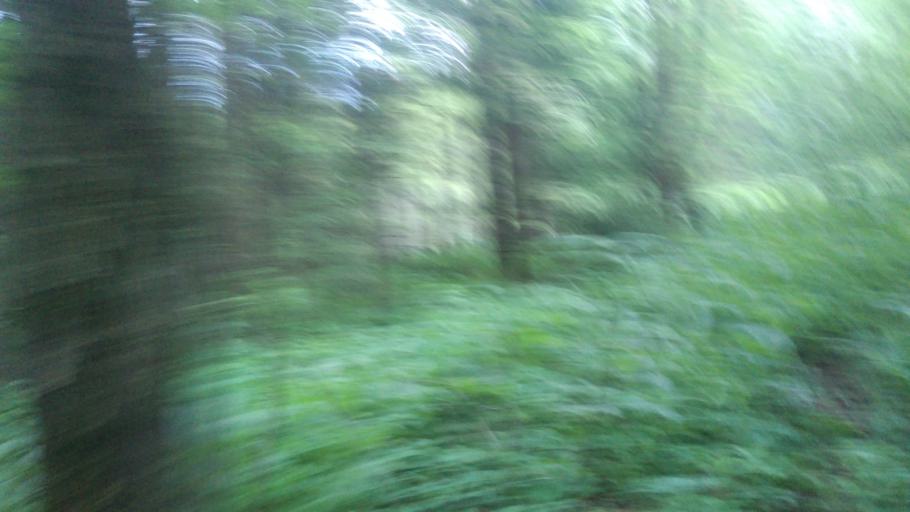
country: RU
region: Perm
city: Froly
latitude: 57.9611
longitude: 56.3070
